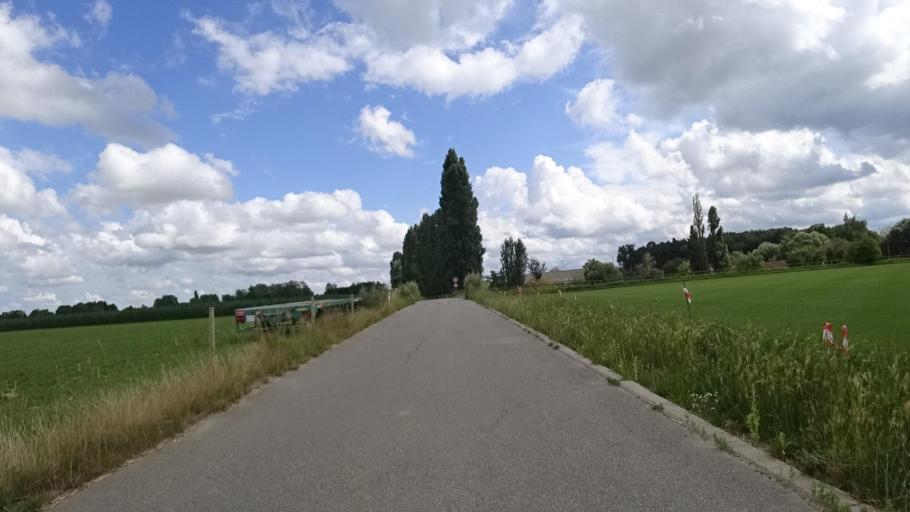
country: BE
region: Wallonia
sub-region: Province du Brabant Wallon
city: Villers-la-Ville
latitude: 50.5591
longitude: 4.5047
